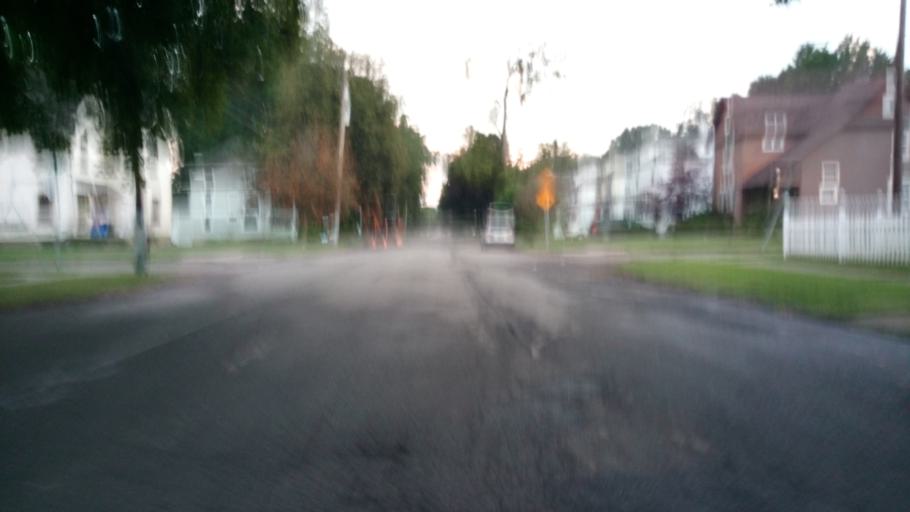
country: US
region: New York
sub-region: Chemung County
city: Elmira
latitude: 42.0938
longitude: -76.8238
